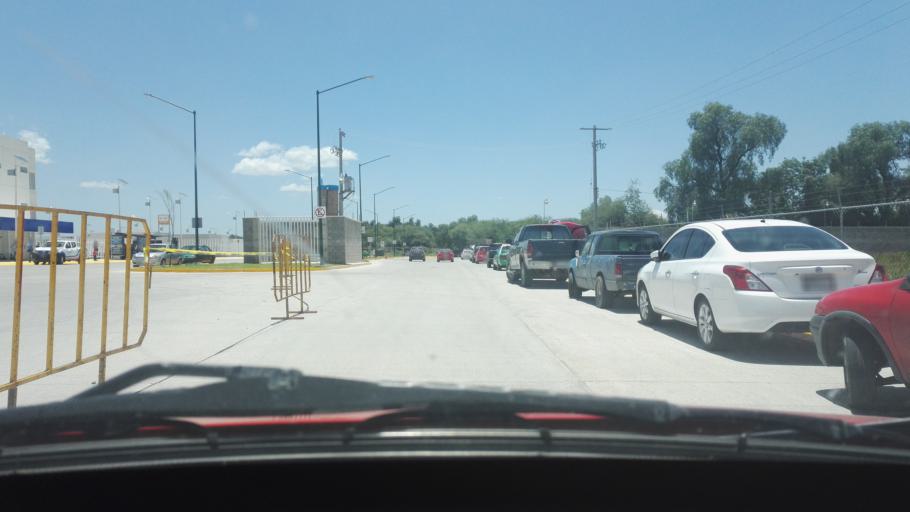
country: MX
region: Guanajuato
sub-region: Leon
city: Ladrilleras del Refugio
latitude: 21.0586
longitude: -101.5670
